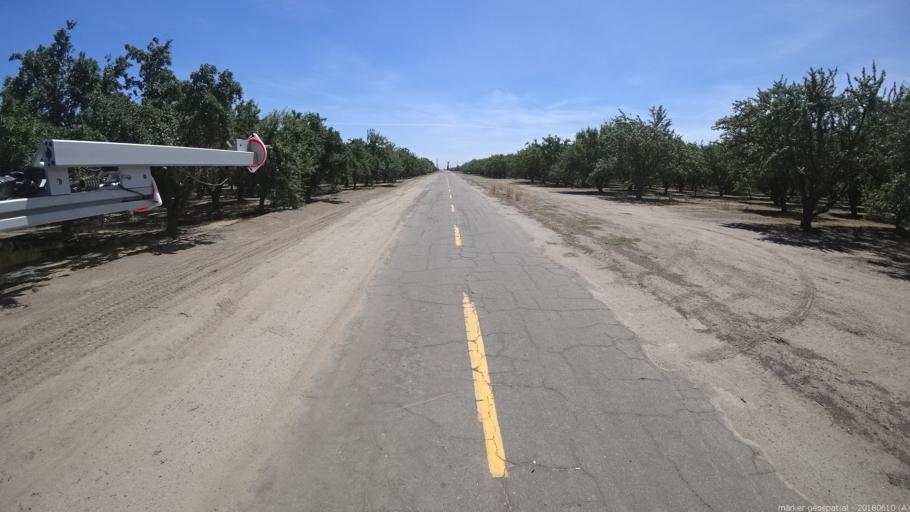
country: US
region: California
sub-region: Madera County
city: Chowchilla
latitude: 37.0398
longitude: -120.3864
